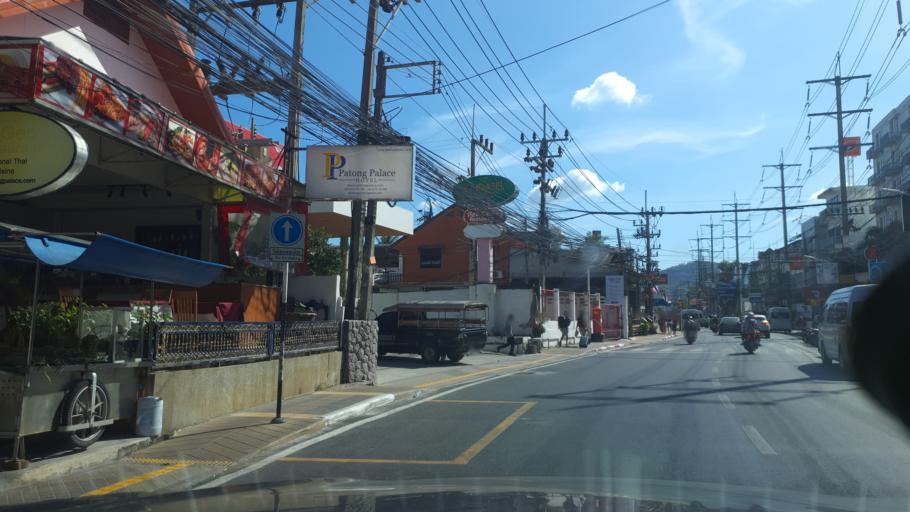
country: TH
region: Phuket
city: Patong
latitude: 7.9017
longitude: 98.3007
